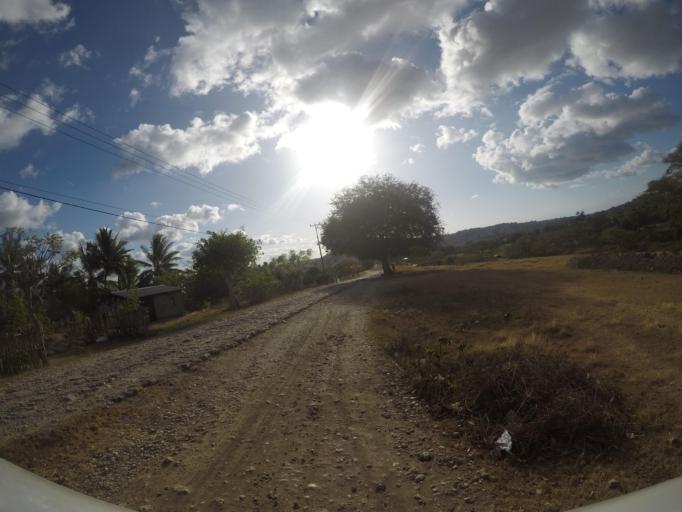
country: TL
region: Lautem
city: Lospalos
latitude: -8.4282
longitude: 126.8392
